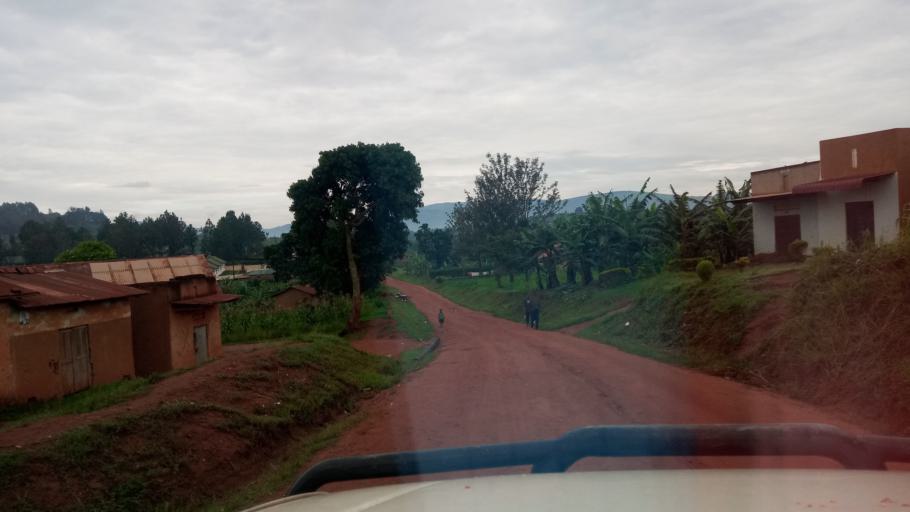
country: UG
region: Western Region
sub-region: Buhweju District
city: Buhweju
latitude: -0.1693
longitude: 30.4636
